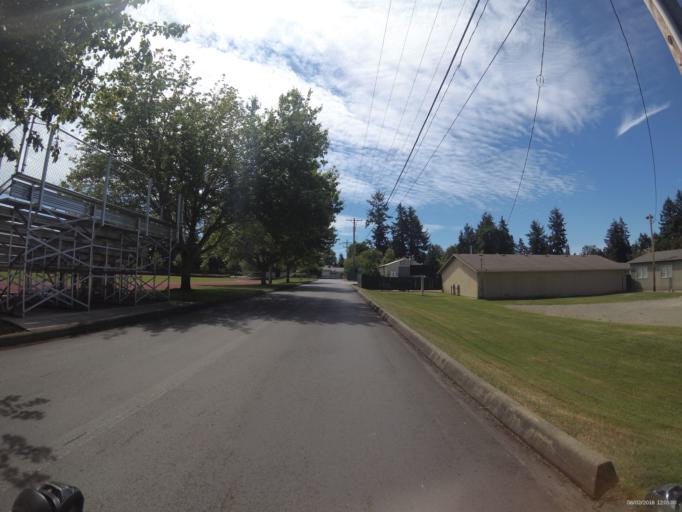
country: US
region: Washington
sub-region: Pierce County
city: University Place
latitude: 47.2000
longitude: -122.5458
